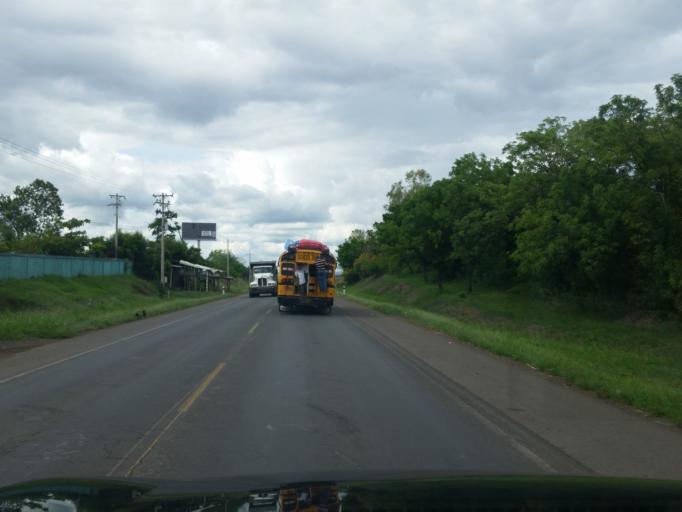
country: NI
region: Managua
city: Tipitapa
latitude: 12.2384
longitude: -86.0916
